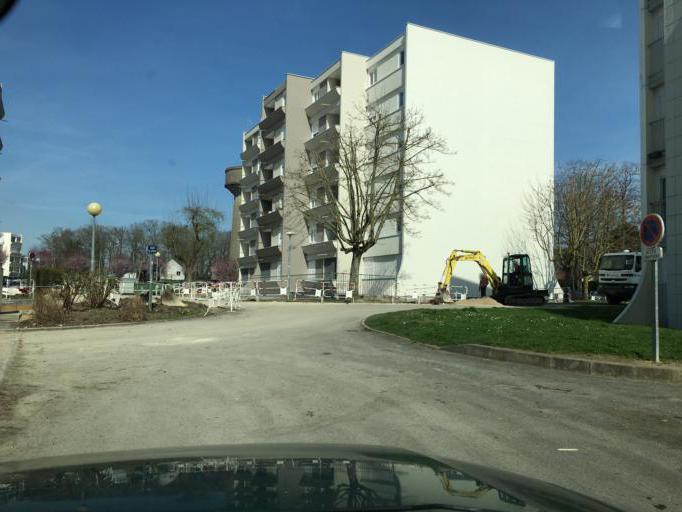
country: FR
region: Centre
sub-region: Departement du Loiret
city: Saran
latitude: 47.9547
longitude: 1.8778
